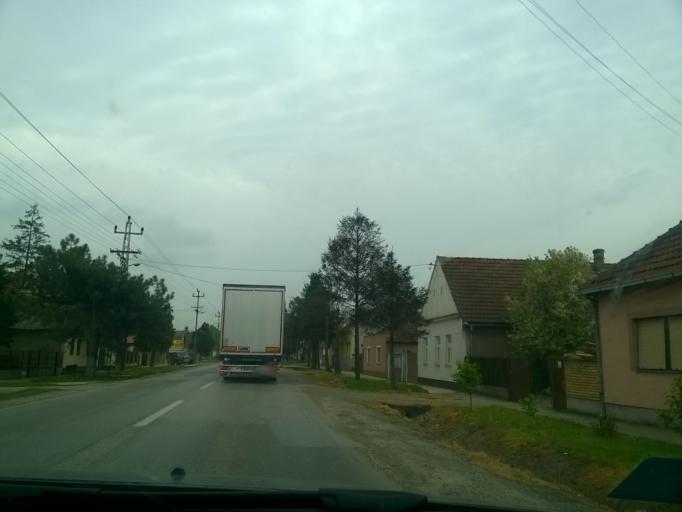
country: RS
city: Hrtkovci
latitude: 44.8801
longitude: 19.7666
